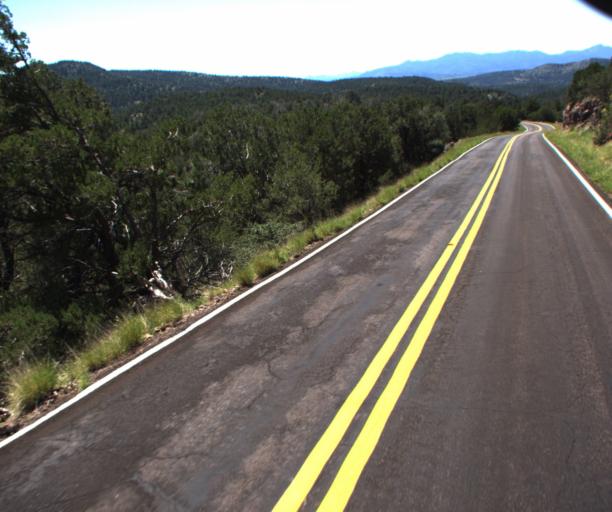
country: US
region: Arizona
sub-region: Greenlee County
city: Morenci
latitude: 33.3906
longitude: -109.3318
